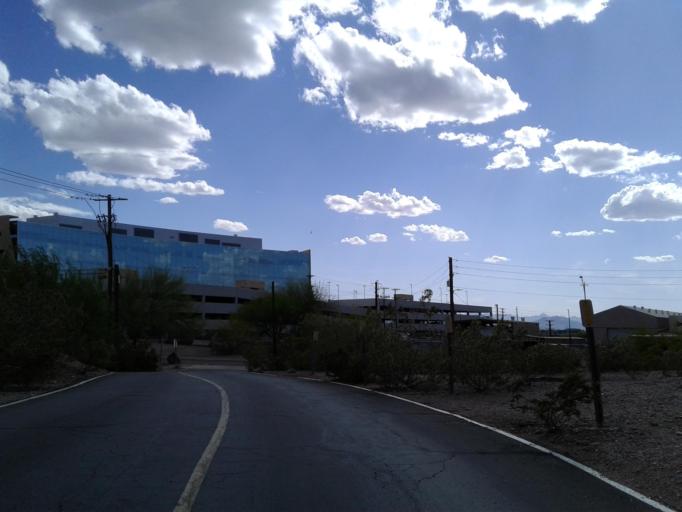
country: US
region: Arizona
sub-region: Maricopa County
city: Tempe Junction
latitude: 33.4397
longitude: -111.9436
